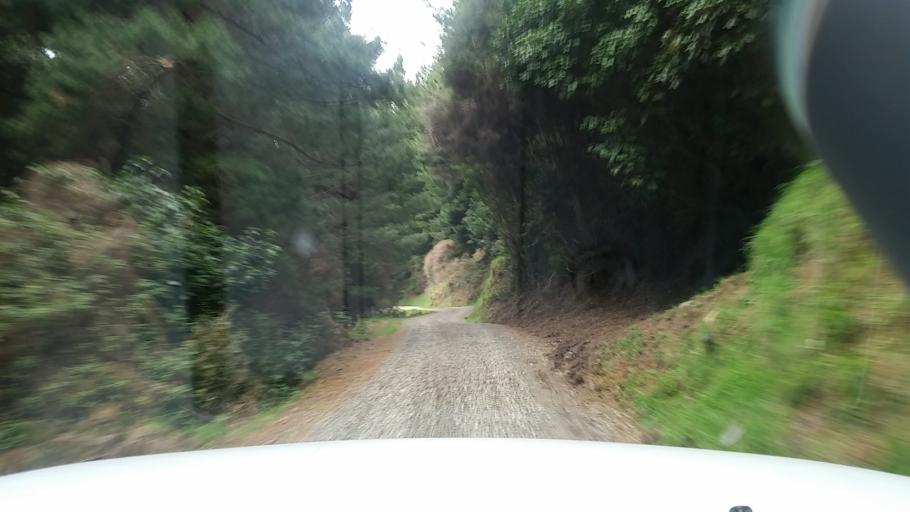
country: NZ
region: Canterbury
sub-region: Christchurch City
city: Christchurch
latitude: -43.6968
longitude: 172.7798
